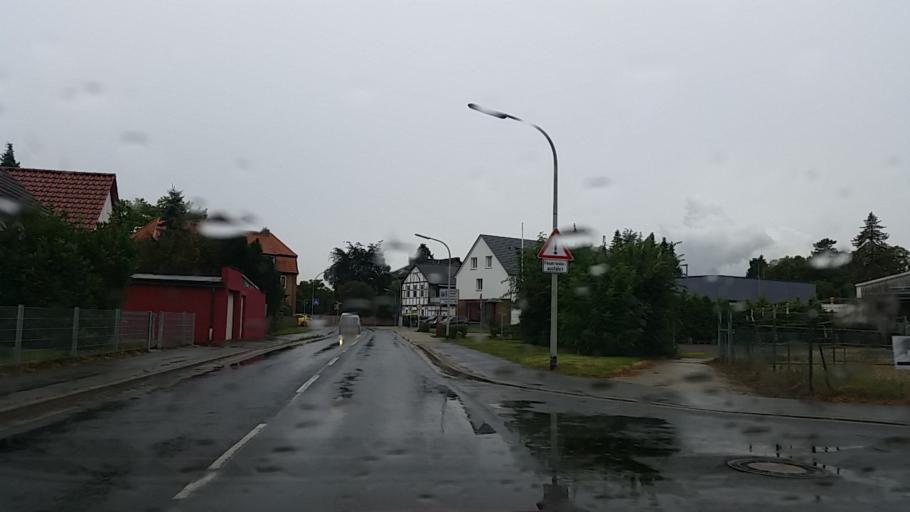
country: DE
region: Lower Saxony
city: Leiferde
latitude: 52.2055
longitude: 10.5089
